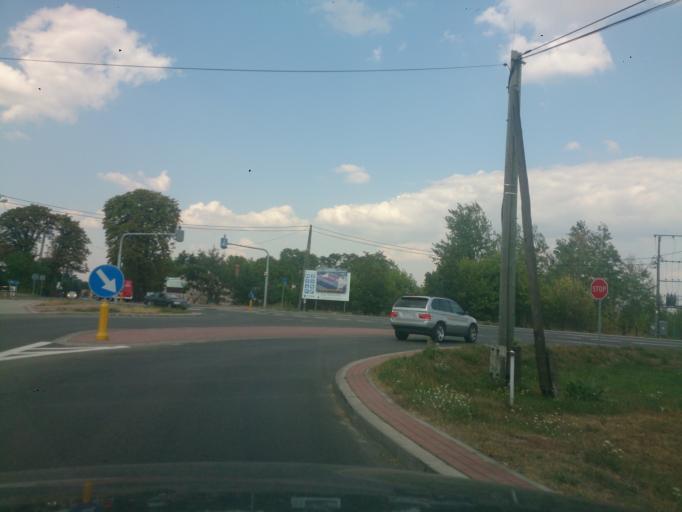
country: PL
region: Subcarpathian Voivodeship
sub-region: Powiat tarnobrzeski
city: Baranow Sandomierski
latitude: 50.4940
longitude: 21.5455
